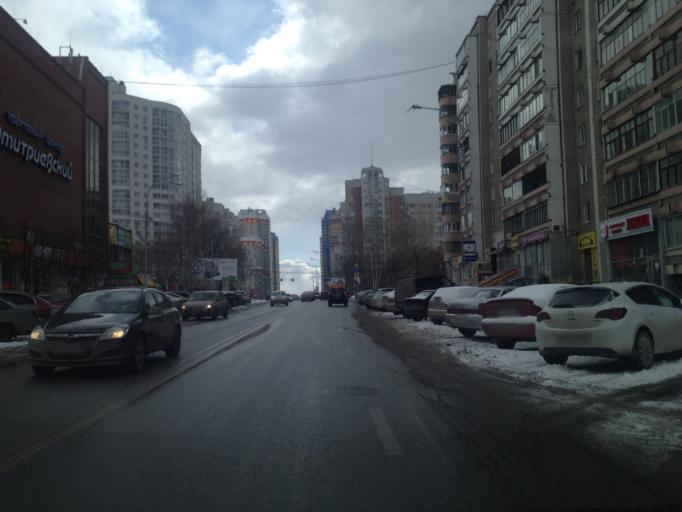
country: RU
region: Sverdlovsk
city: Yekaterinburg
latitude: 56.8088
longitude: 60.6010
